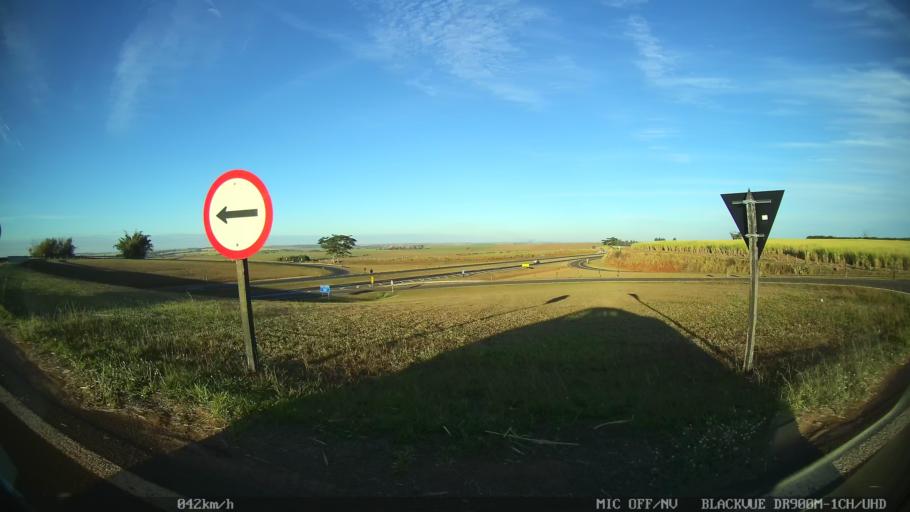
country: BR
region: Sao Paulo
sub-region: Catanduva
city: Catanduva
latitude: -21.0503
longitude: -49.1302
